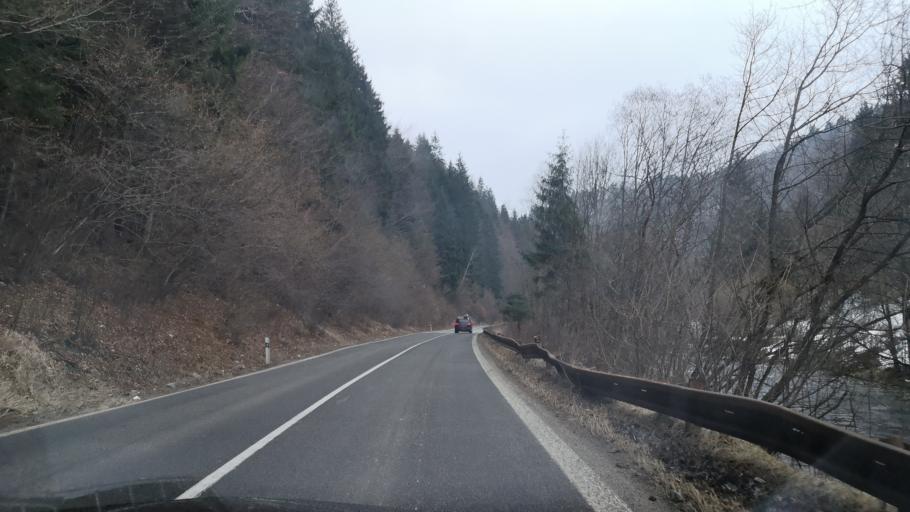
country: SK
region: Zilinsky
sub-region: Okres Dolny Kubin
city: Dolny Kubin
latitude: 49.2067
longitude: 19.1728
